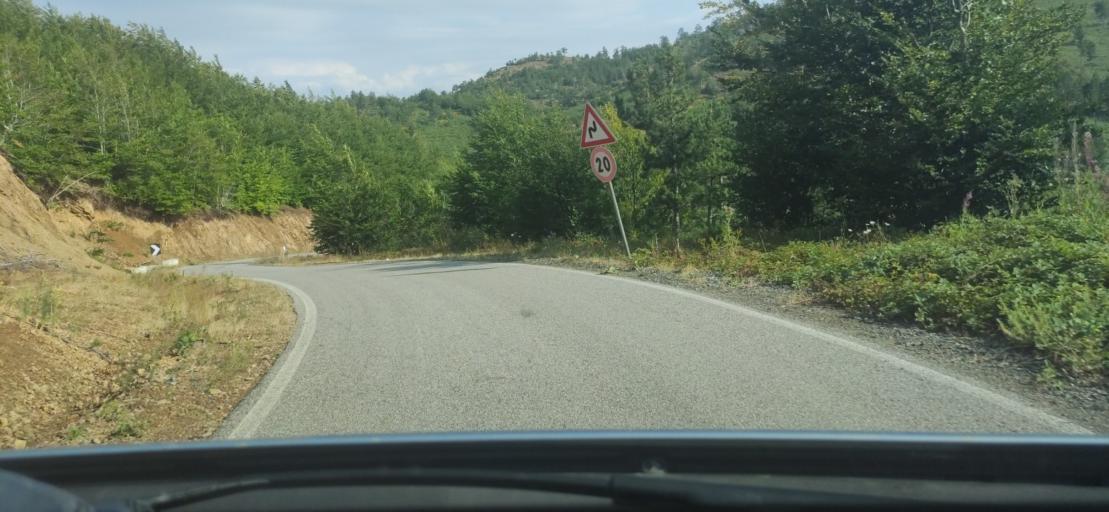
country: AL
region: Shkoder
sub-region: Rrethi i Pukes
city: Iballe
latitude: 42.1744
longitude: 20.0257
